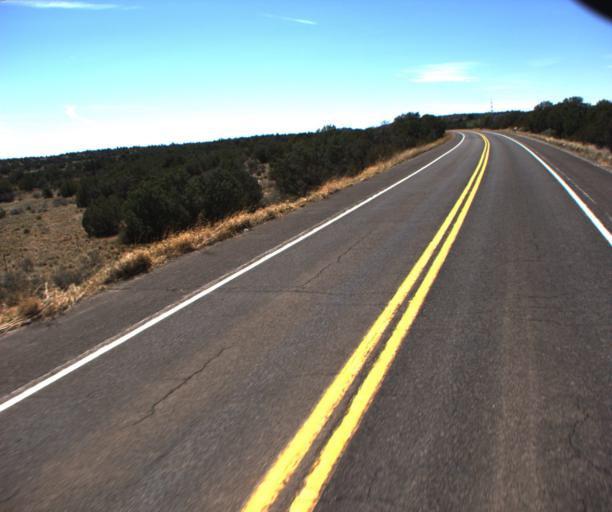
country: US
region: Arizona
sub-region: Mohave County
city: Peach Springs
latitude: 35.5540
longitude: -113.3734
